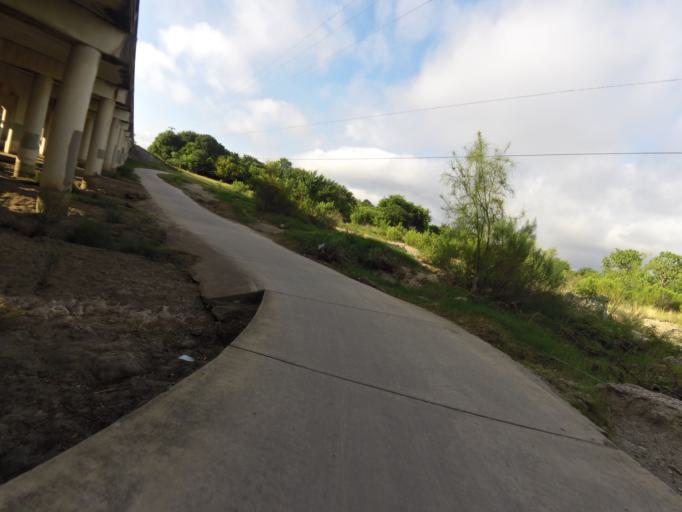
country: US
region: Texas
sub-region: Bexar County
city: Leon Valley
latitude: 29.5127
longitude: -98.6328
